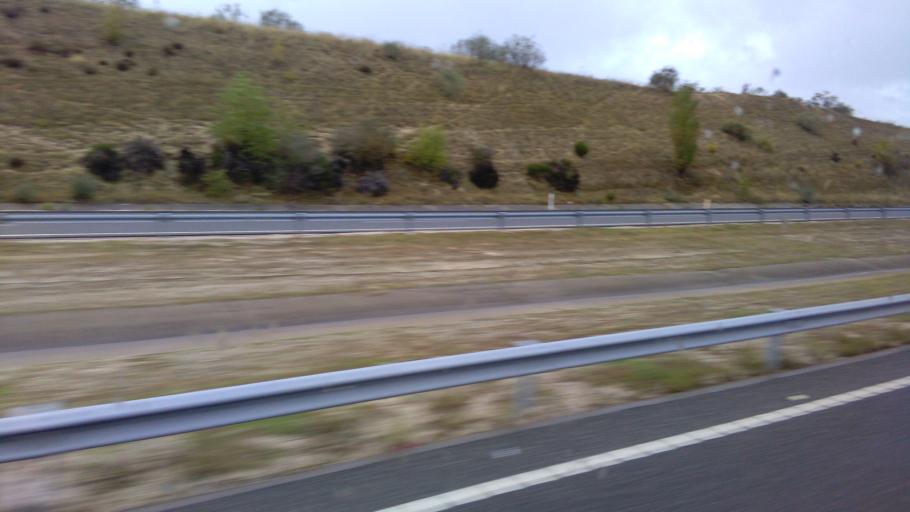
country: ES
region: Madrid
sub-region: Provincia de Madrid
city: Arroyomolinos
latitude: 40.2576
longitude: -3.9318
